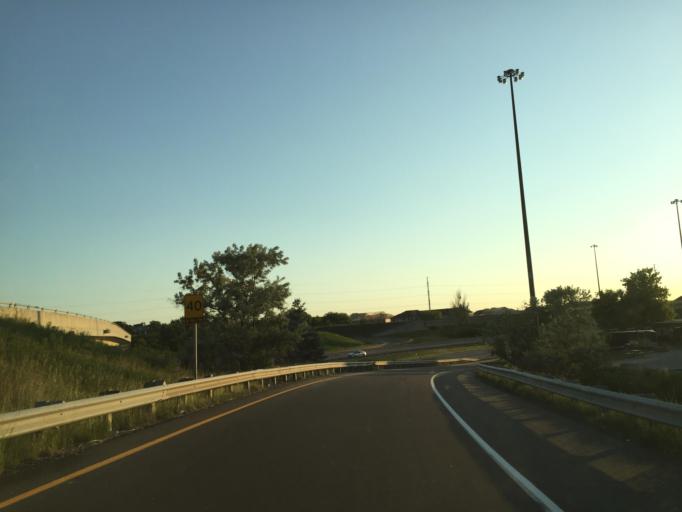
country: CA
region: Ontario
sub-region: Wellington County
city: Guelph
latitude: 43.5276
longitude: -80.2639
